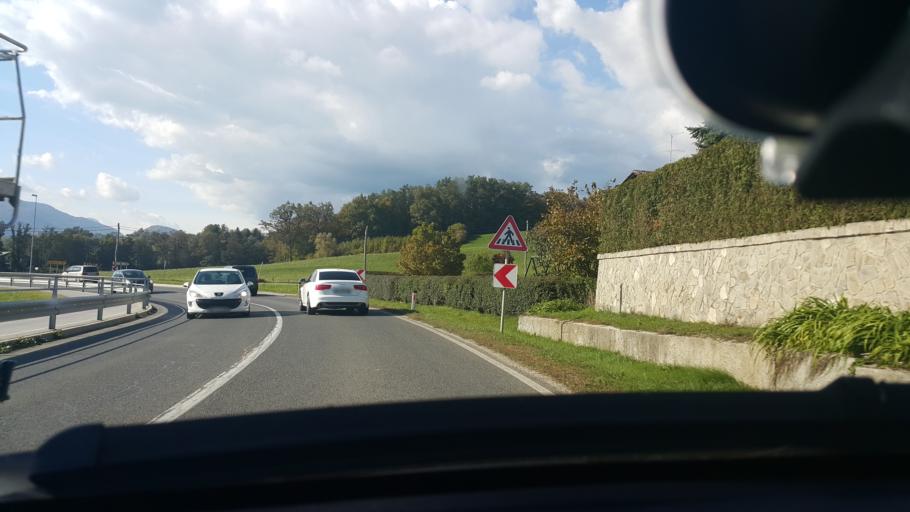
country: SI
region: Slovenska Konjice
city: Slovenske Konjice
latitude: 46.3429
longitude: 15.4549
